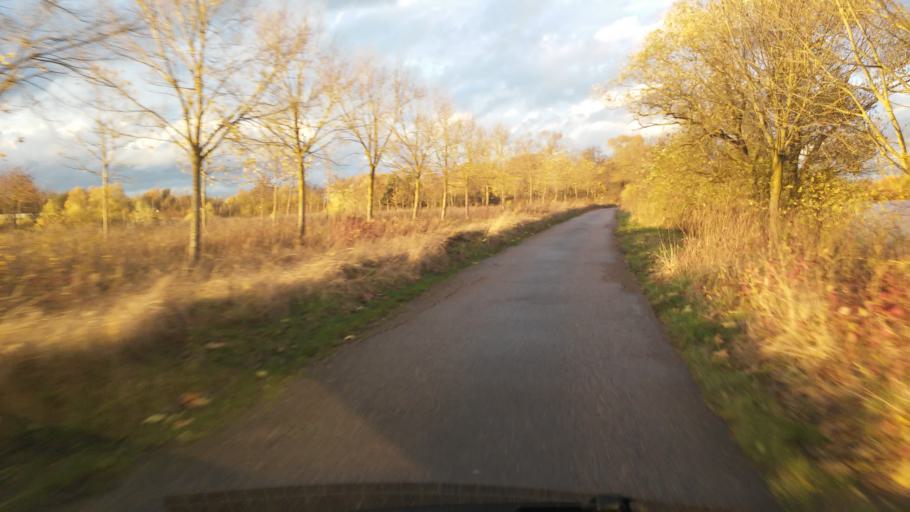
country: FR
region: Lorraine
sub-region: Departement de la Moselle
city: Talange
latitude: 49.2341
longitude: 6.1862
